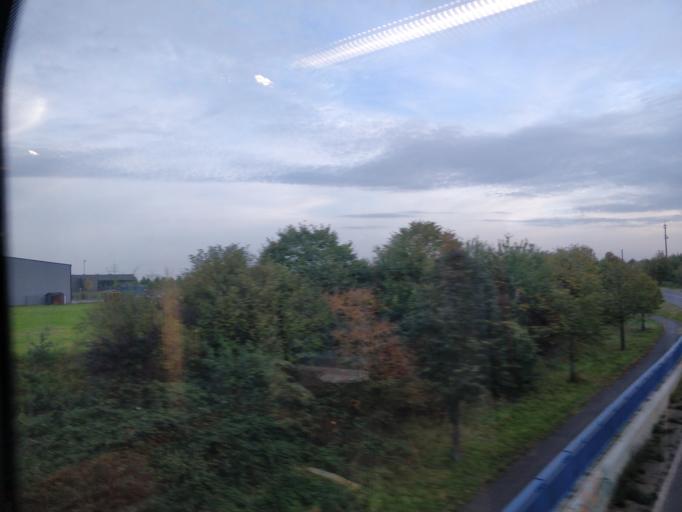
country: DE
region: North Rhine-Westphalia
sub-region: Regierungsbezirk Dusseldorf
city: Dormagen
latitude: 51.1390
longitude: 6.7616
